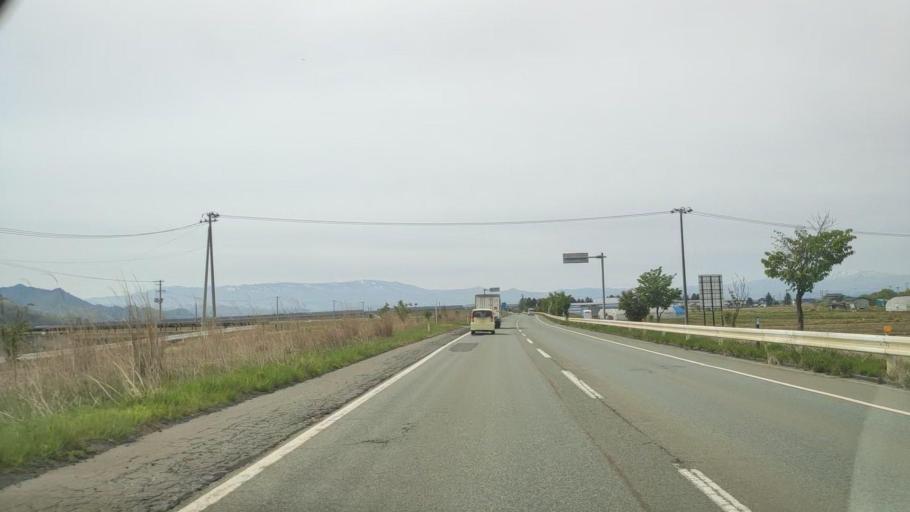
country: JP
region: Yamagata
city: Takahata
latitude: 38.0359
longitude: 140.1730
